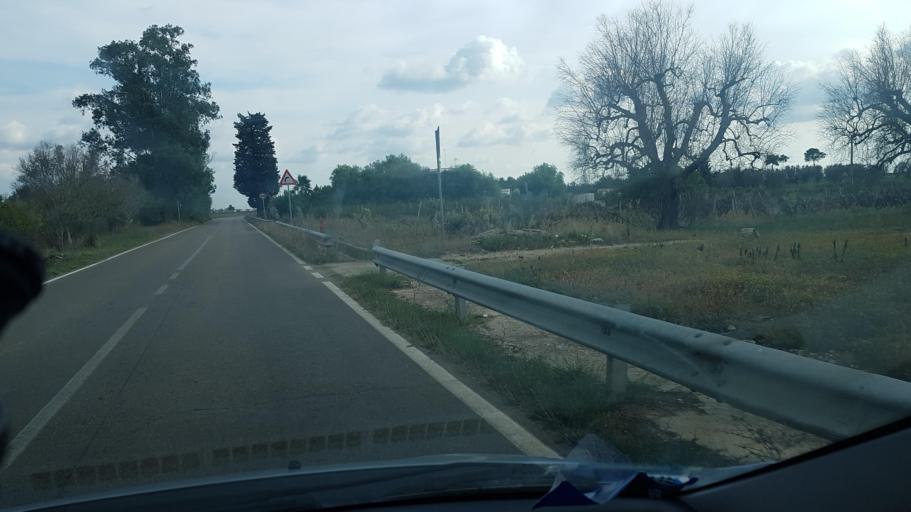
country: IT
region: Apulia
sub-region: Provincia di Brindisi
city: Cellino San Marco
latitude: 40.4449
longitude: 17.9541
